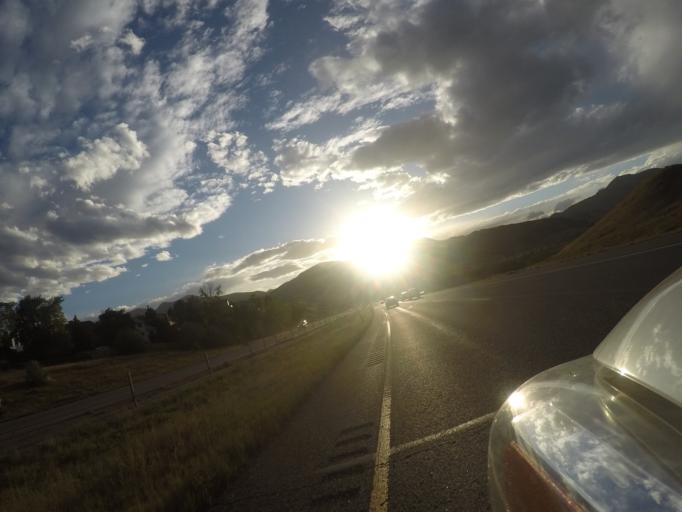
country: US
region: Colorado
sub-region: Jefferson County
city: Ken Caryl
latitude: 39.6389
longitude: -105.1510
